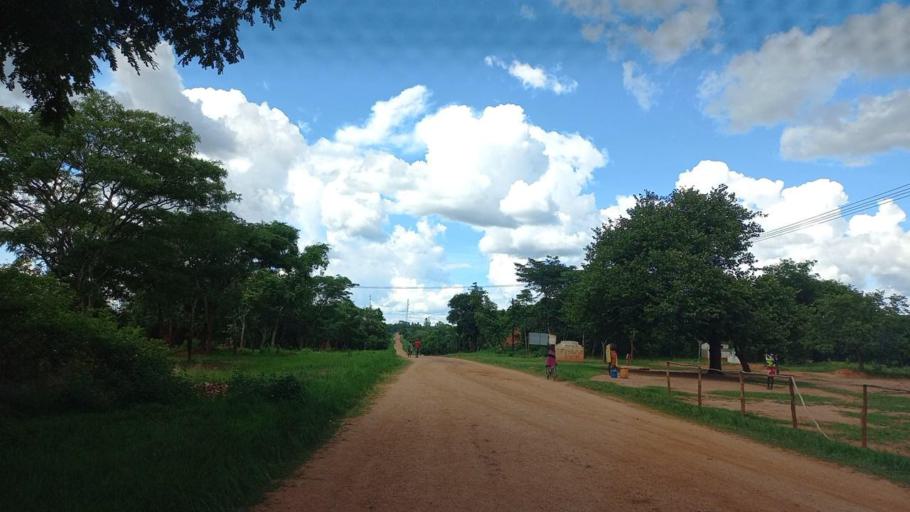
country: ZM
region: North-Western
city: Mwinilunga
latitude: -12.0787
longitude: 24.3007
